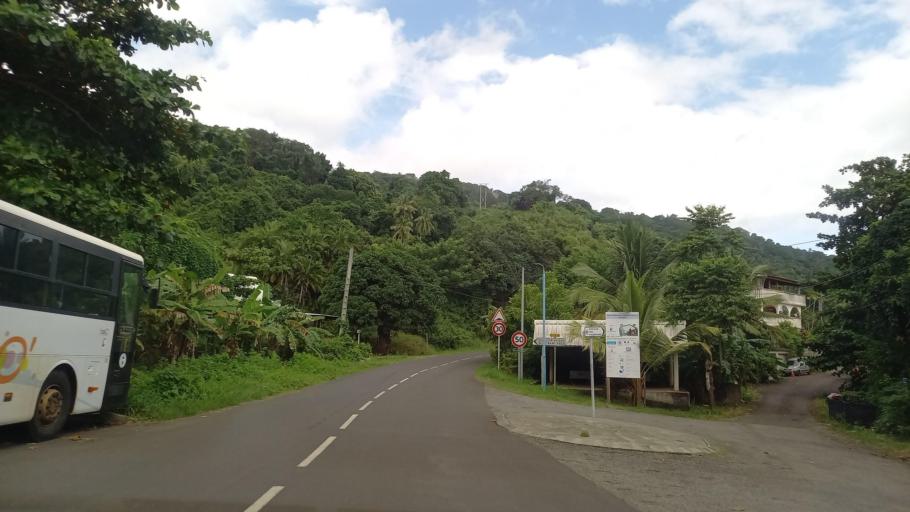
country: YT
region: Kani-Keli
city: Kani Keli
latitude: -12.9426
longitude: 45.1024
